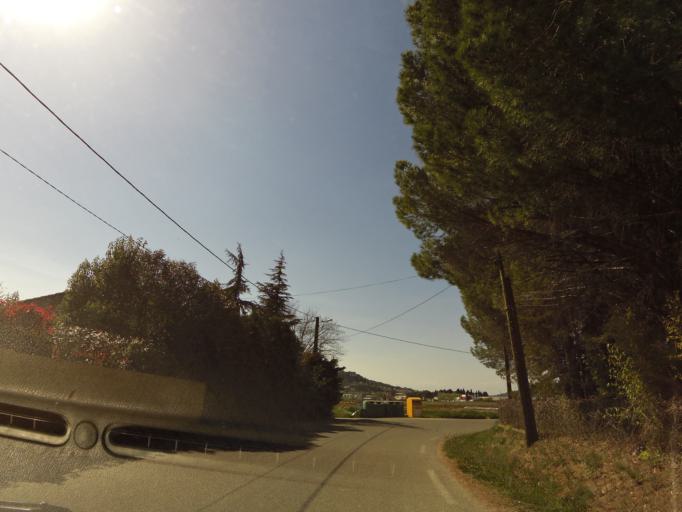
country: FR
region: Languedoc-Roussillon
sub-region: Departement du Gard
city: Calvisson
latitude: 43.7792
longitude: 4.2069
